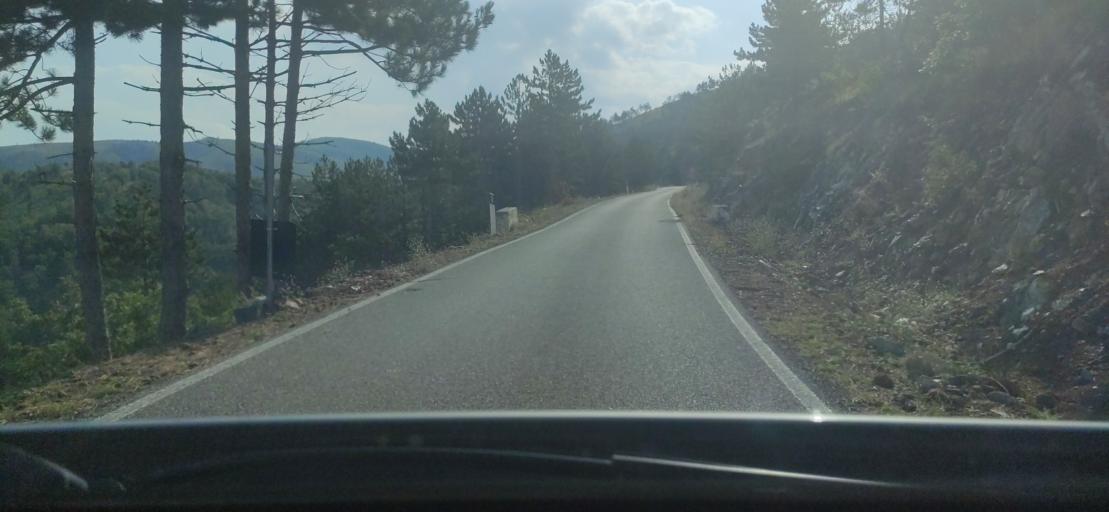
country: AL
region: Shkoder
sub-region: Rrethi i Pukes
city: Iballe
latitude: 42.1711
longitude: 20.0173
